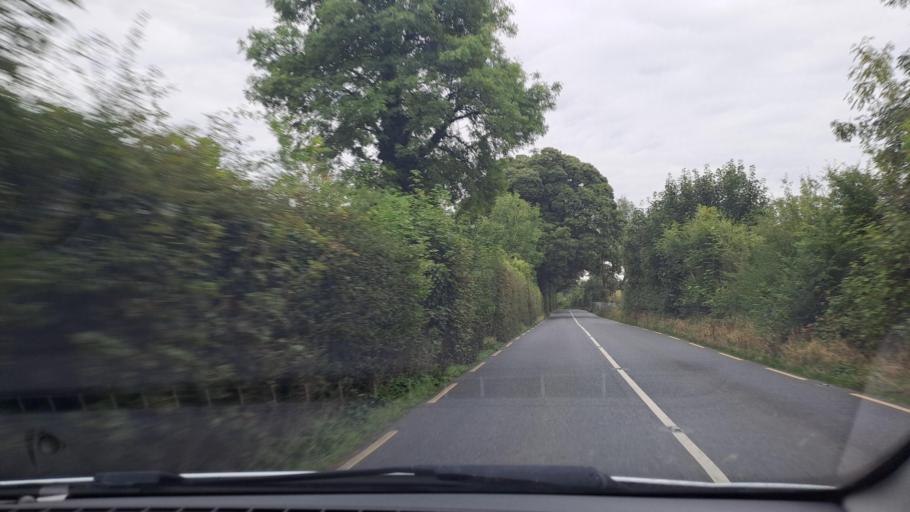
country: IE
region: Ulster
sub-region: County Monaghan
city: Carrickmacross
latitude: 53.9928
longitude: -6.7745
